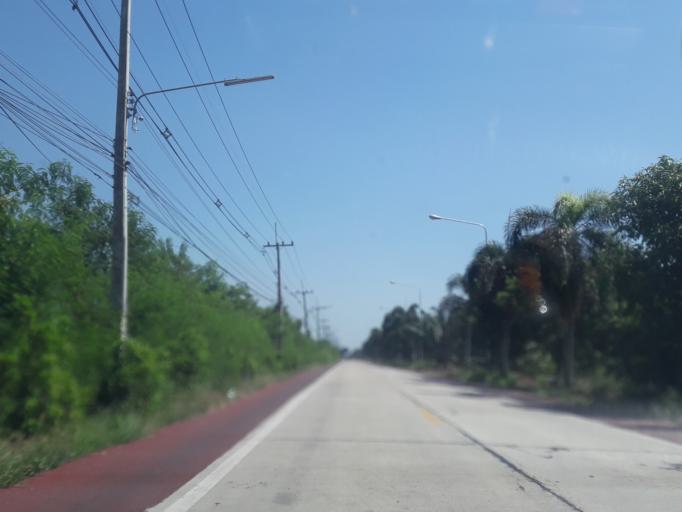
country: TH
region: Pathum Thani
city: Nong Suea
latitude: 14.1365
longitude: 100.8538
